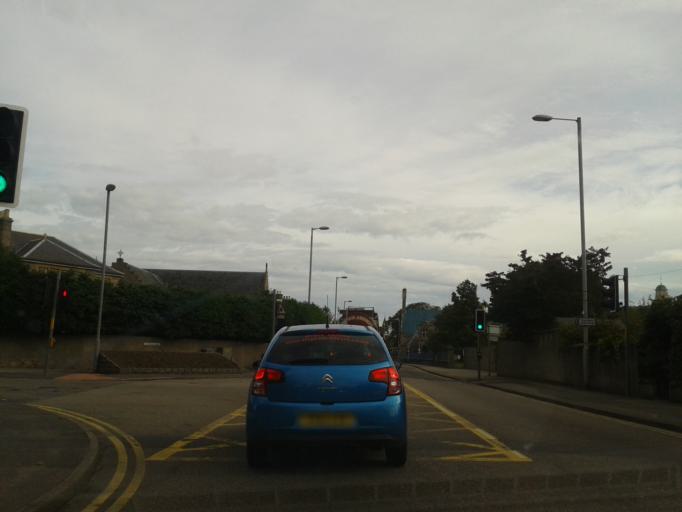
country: GB
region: Scotland
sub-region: Highland
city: Nairn
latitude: 57.5836
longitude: -3.8754
